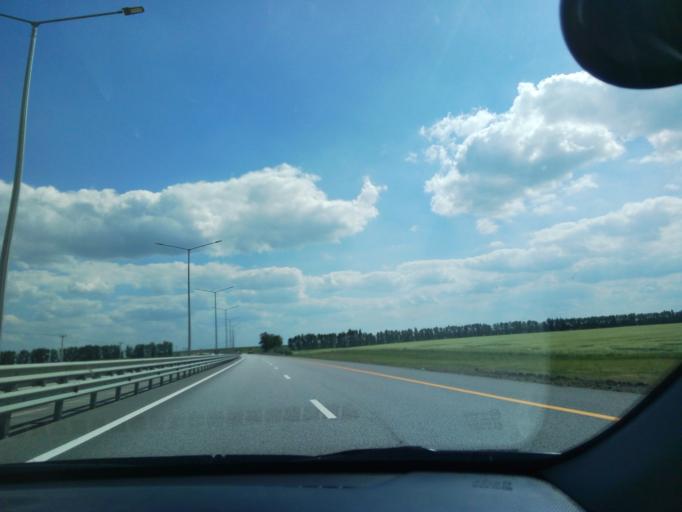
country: RU
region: Voronezj
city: Podkletnoye
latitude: 51.5207
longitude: 39.5107
